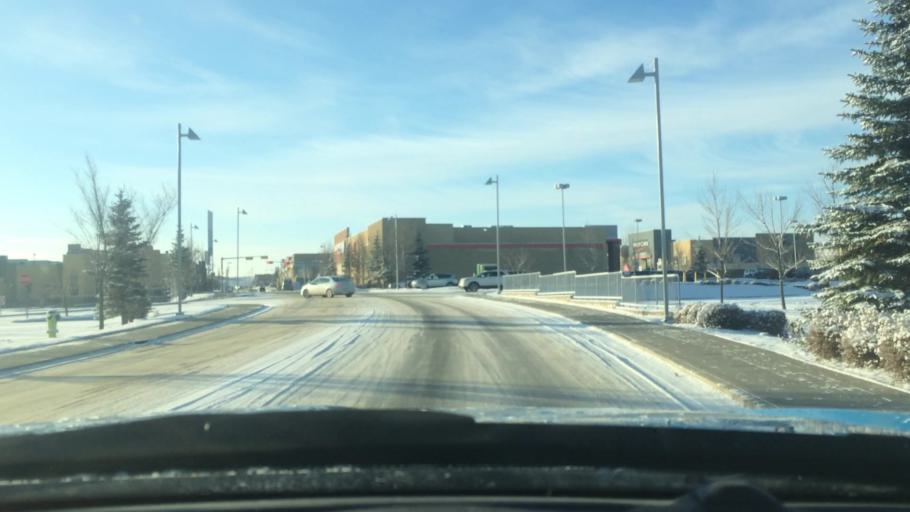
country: CA
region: Alberta
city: Calgary
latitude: 51.1589
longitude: -114.1600
